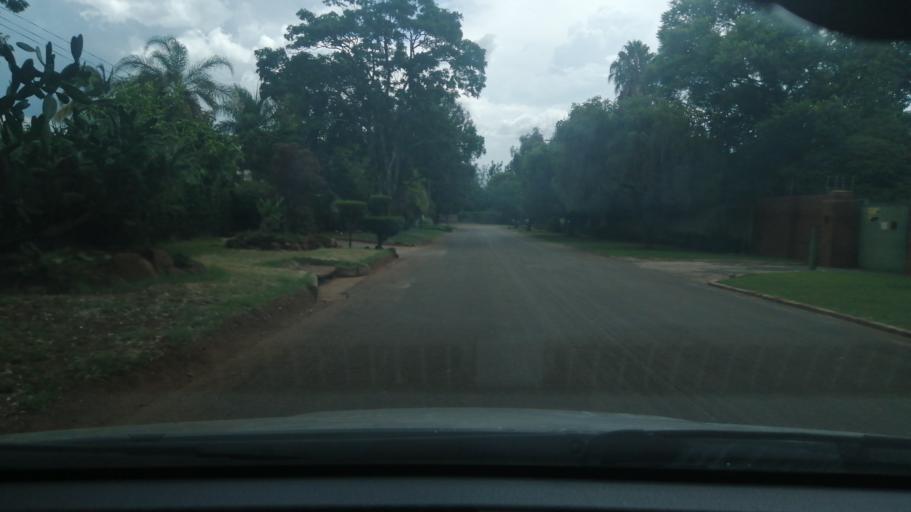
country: ZW
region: Harare
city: Harare
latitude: -17.7936
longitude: 31.0662
